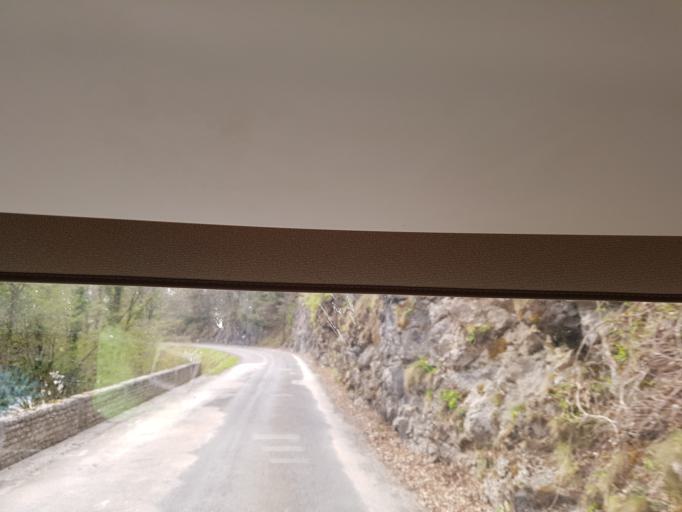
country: FR
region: Languedoc-Roussillon
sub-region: Departement de l'Aude
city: Quillan
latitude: 42.7701
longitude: 2.1163
